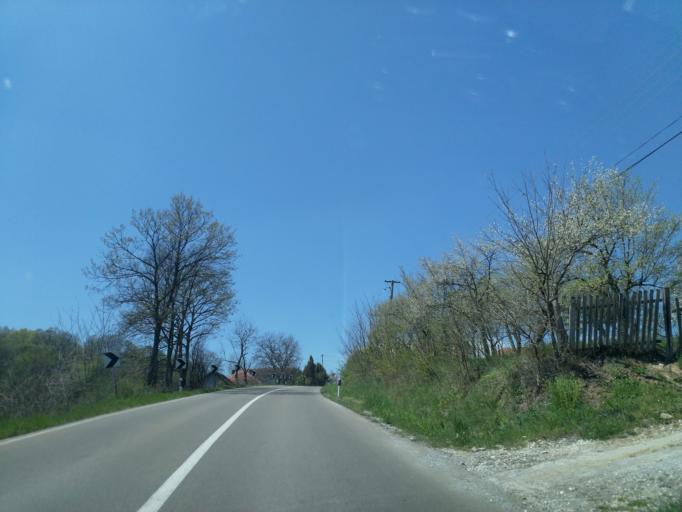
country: RS
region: Central Serbia
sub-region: Belgrade
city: Lazarevac
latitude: 44.3478
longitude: 20.3899
